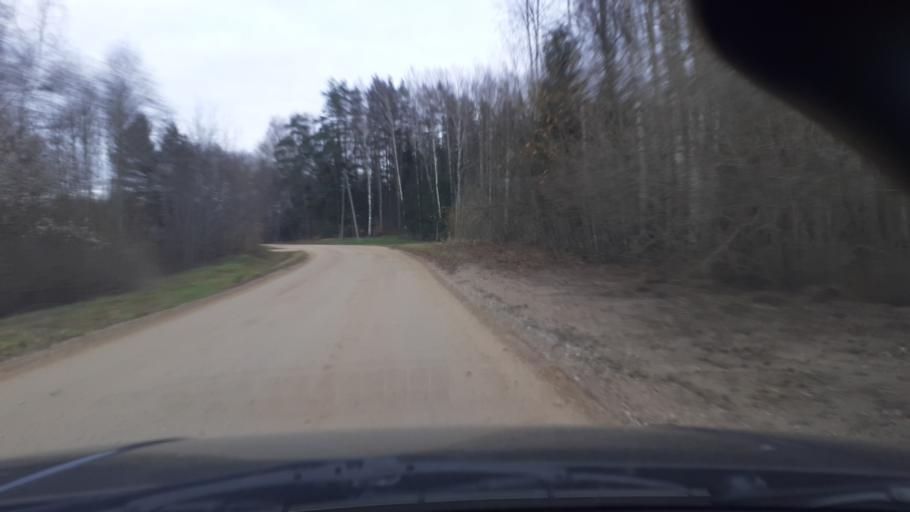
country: LV
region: Alsunga
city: Alsunga
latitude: 56.9471
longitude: 21.6403
